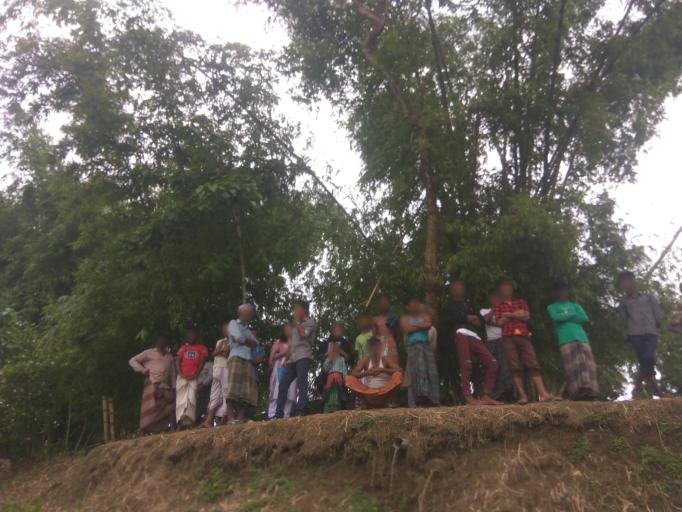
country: IN
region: Assam
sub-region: Karimganj
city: Karimganj
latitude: 24.8535
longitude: 92.1450
